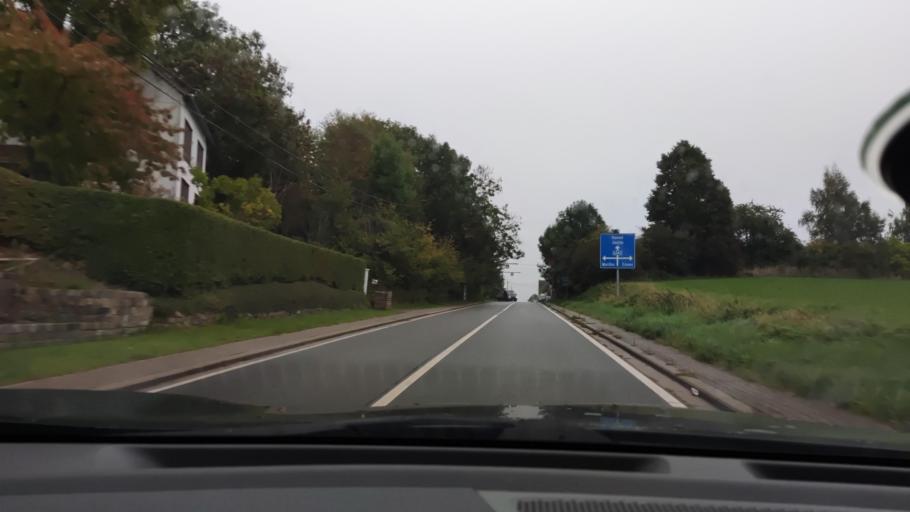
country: BE
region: Wallonia
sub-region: Province du Brabant Wallon
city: Jodoigne
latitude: 50.7000
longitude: 4.9262
